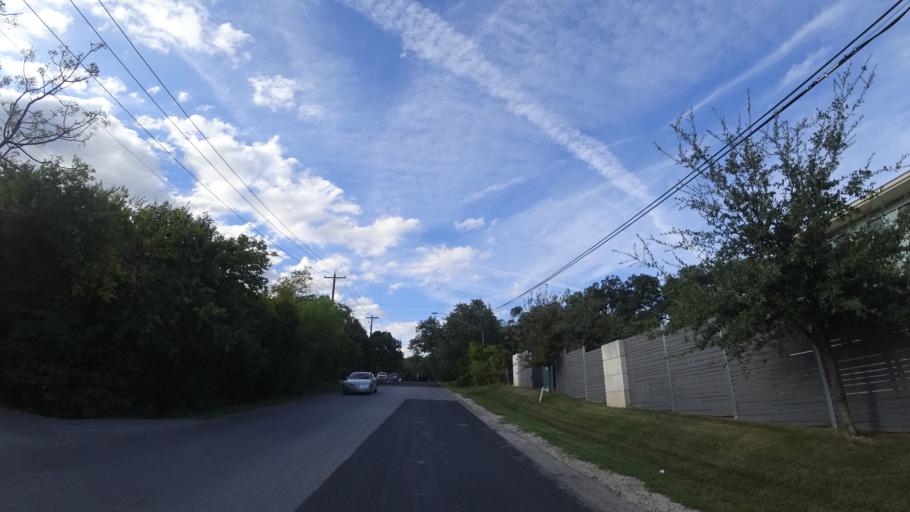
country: US
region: Texas
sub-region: Travis County
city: Onion Creek
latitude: 30.1958
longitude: -97.7730
